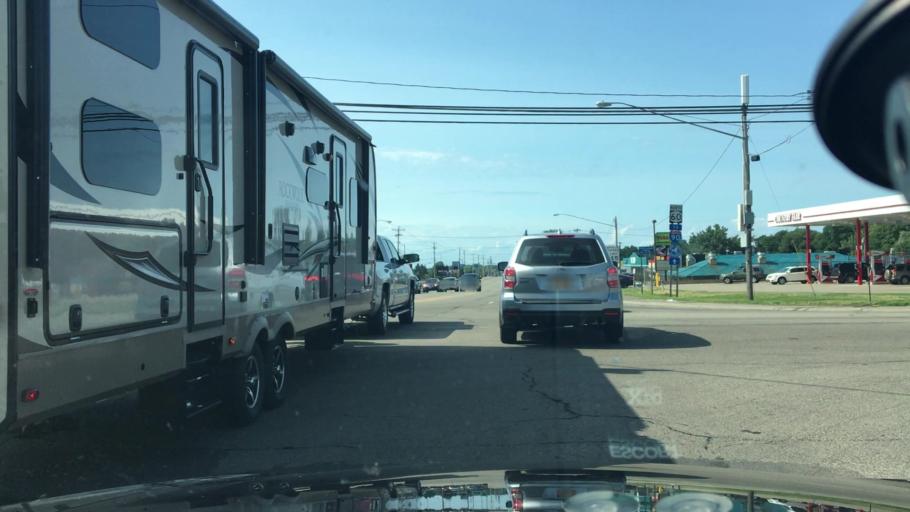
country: US
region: New York
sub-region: Chautauqua County
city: Fredonia
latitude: 42.4504
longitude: -79.3078
